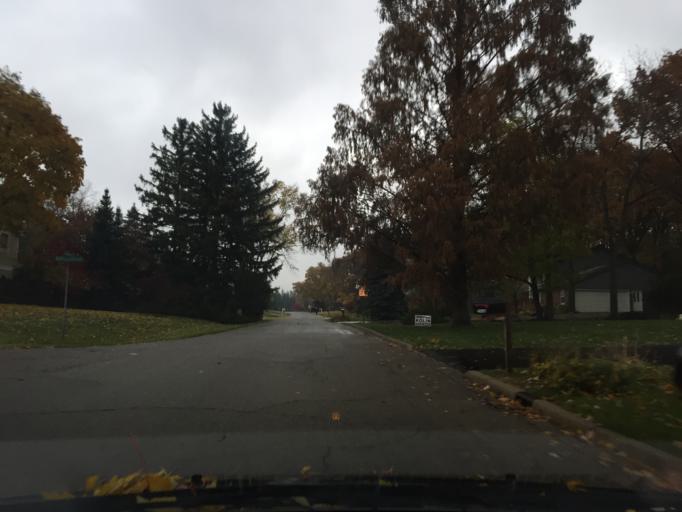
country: US
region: Michigan
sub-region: Oakland County
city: Bloomfield Hills
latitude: 42.5757
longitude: -83.2769
